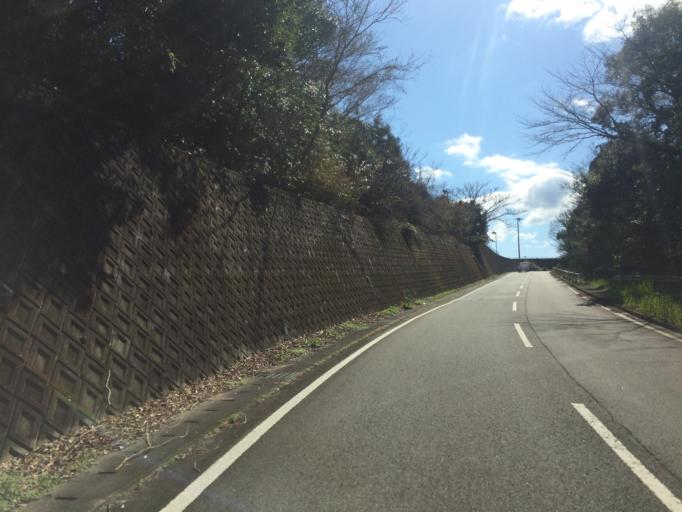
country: JP
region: Shizuoka
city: Shimada
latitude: 34.7578
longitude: 138.1752
